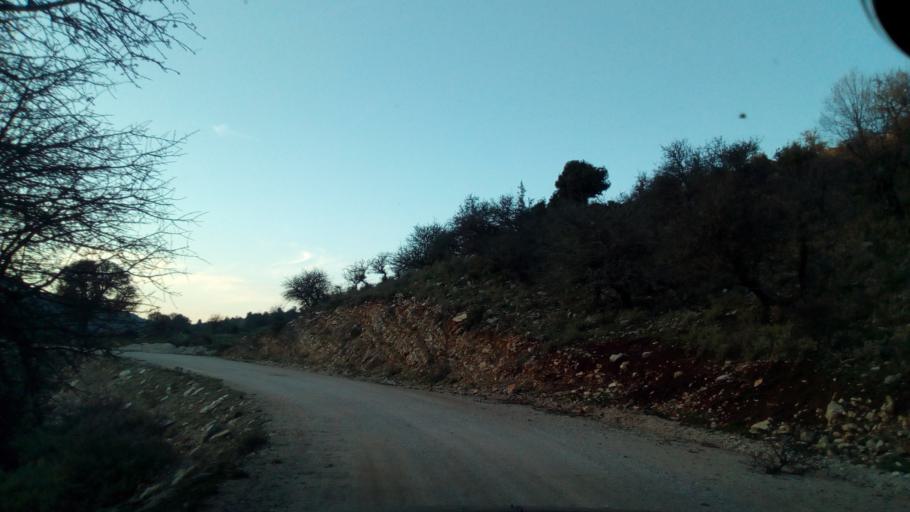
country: GR
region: West Greece
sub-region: Nomos Aitolias kai Akarnanias
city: Nafpaktos
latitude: 38.4598
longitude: 21.8378
